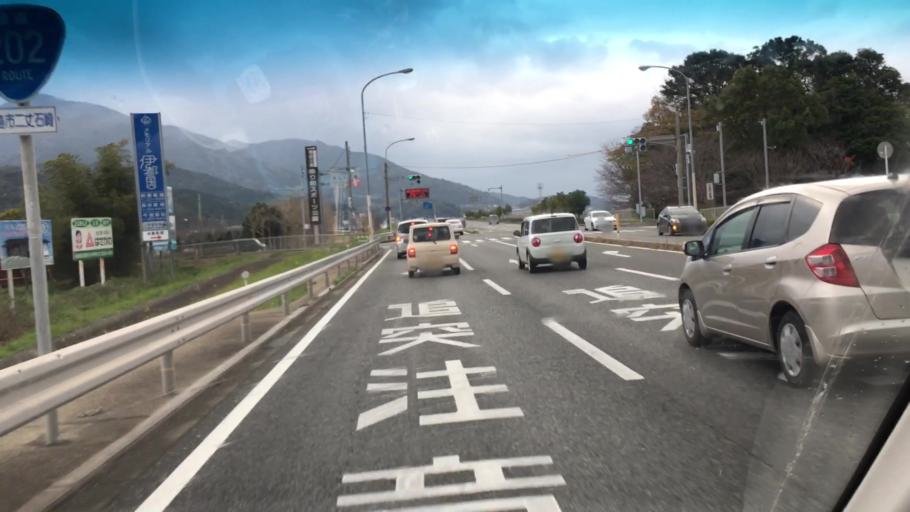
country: JP
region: Fukuoka
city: Maebaru-chuo
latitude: 33.5198
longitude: 130.1613
